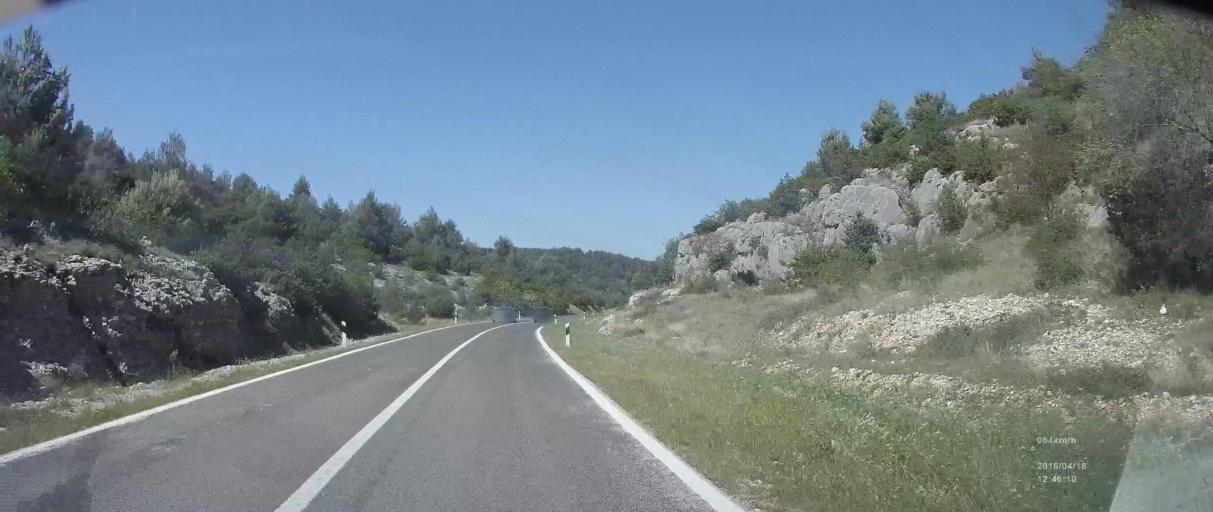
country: HR
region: Sibensko-Kniniska
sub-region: Grad Sibenik
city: Brodarica
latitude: 43.6535
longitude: 16.0573
